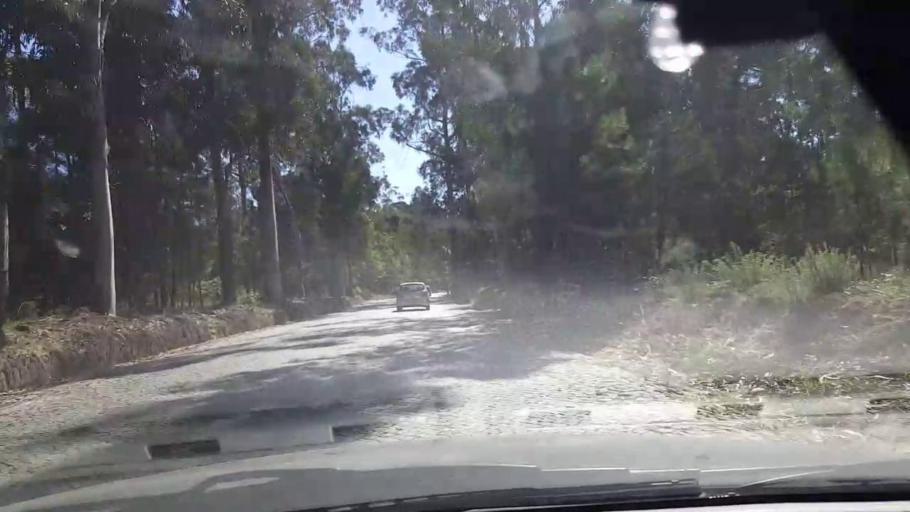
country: PT
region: Porto
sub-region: Vila do Conde
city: Arvore
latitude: 41.3240
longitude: -8.7254
